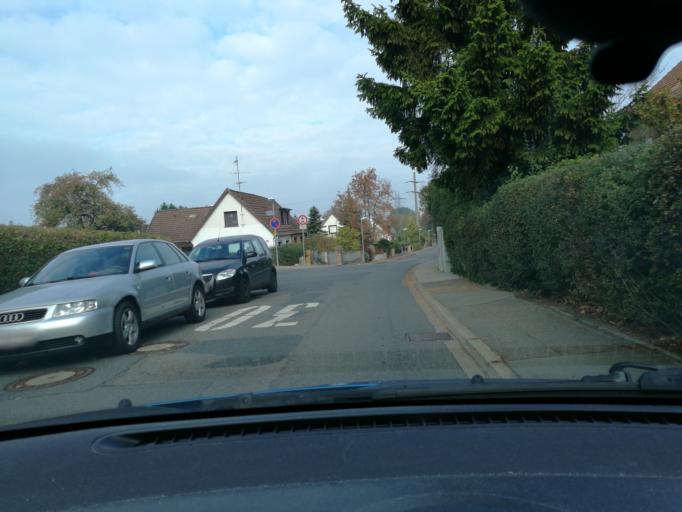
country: DE
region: Lower Saxony
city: Lueneburg
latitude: 53.2656
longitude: 10.4113
